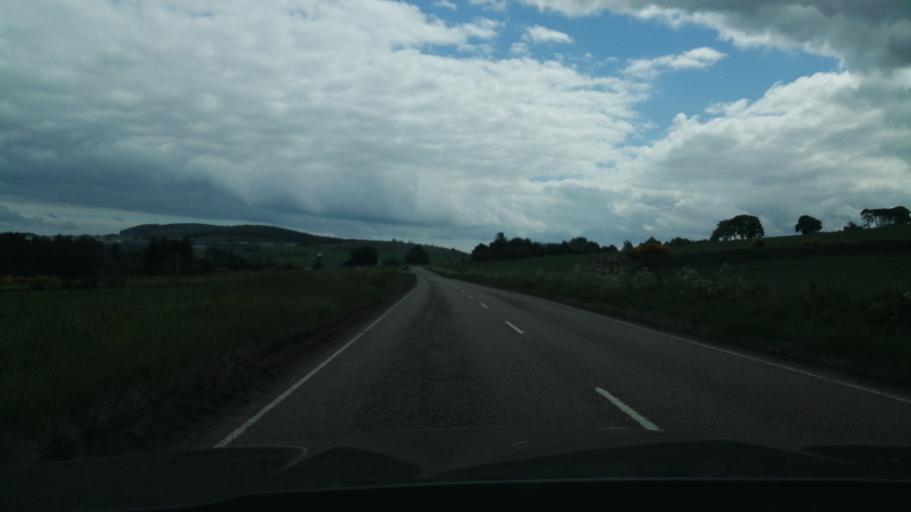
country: GB
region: Scotland
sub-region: Moray
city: Fochabers
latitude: 57.5469
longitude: -3.1007
